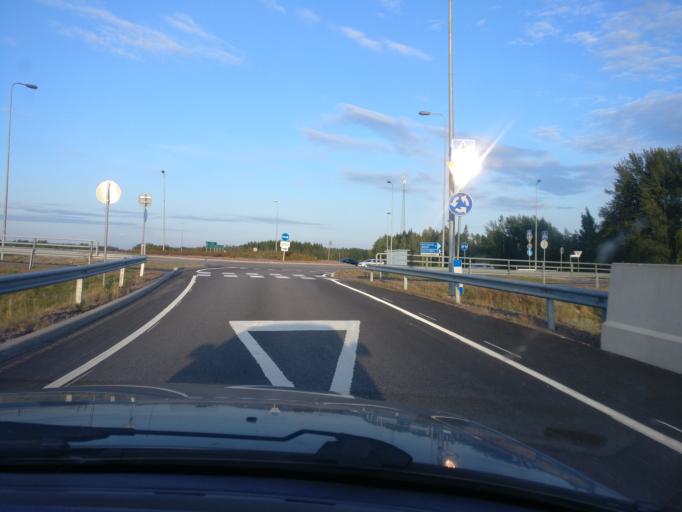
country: FI
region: Kymenlaakso
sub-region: Kotka-Hamina
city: Broby
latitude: 60.5029
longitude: 26.7415
